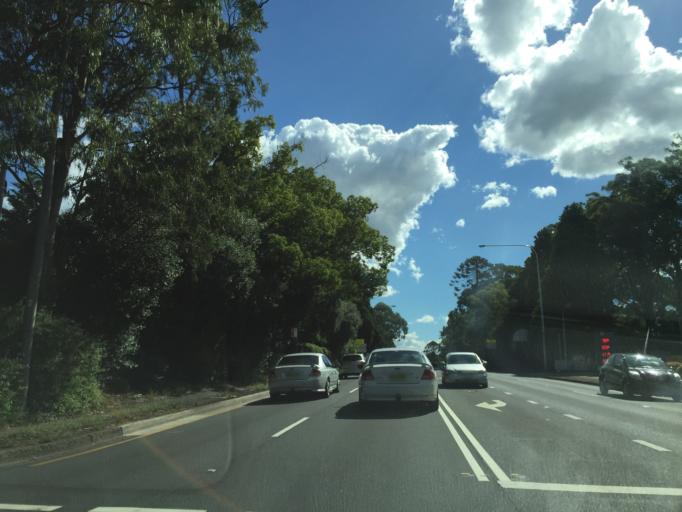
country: AU
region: New South Wales
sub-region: Parramatta
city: Telopea
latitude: -33.7877
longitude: 151.0284
